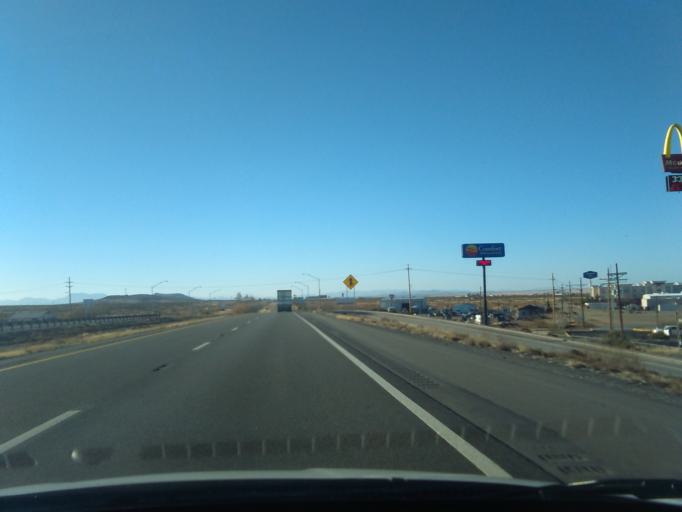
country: US
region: New Mexico
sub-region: Hidalgo County
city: Lordsburg
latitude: 32.3429
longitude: -108.7134
